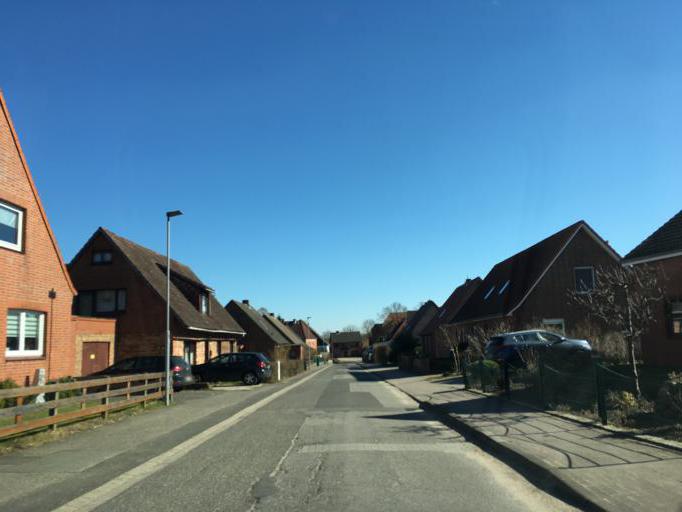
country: DE
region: Schleswig-Holstein
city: Breitenfelde
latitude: 53.6080
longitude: 10.6371
